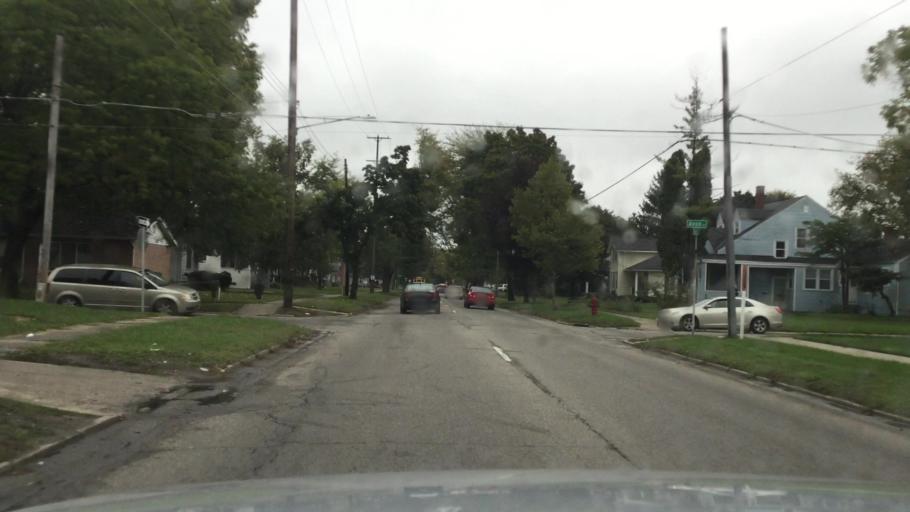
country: US
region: Michigan
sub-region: Saginaw County
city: Saginaw
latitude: 43.4366
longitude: -83.9732
